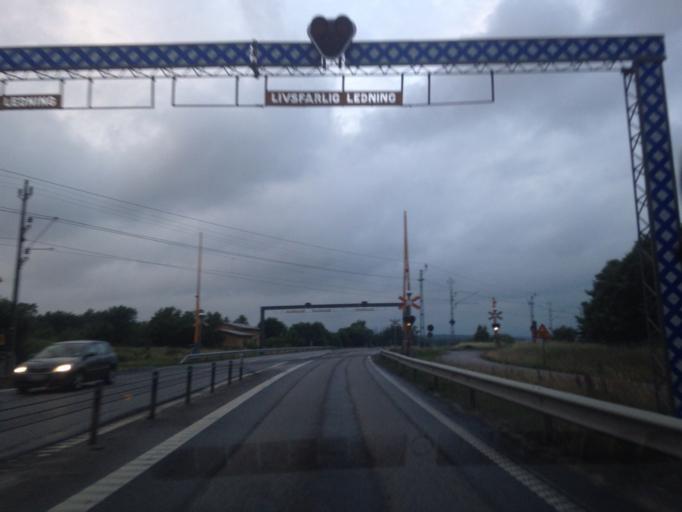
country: SE
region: Halland
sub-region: Varbergs Kommun
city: Varberg
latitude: 57.1276
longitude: 12.2613
